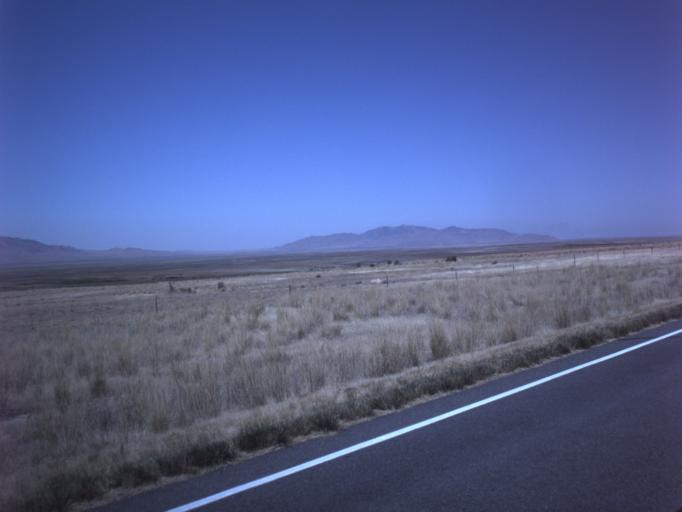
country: US
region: Utah
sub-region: Tooele County
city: Grantsville
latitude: 40.5848
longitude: -112.7234
